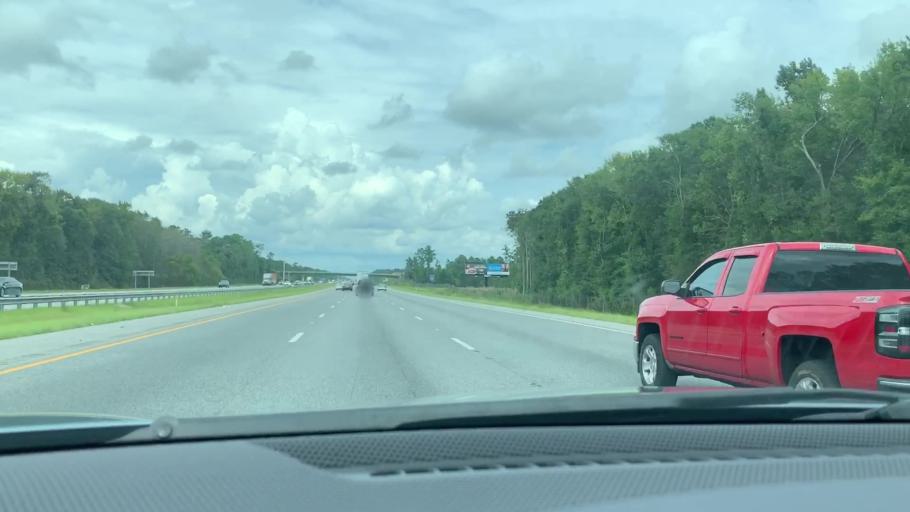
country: US
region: Georgia
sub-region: McIntosh County
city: Darien
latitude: 31.4881
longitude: -81.4468
